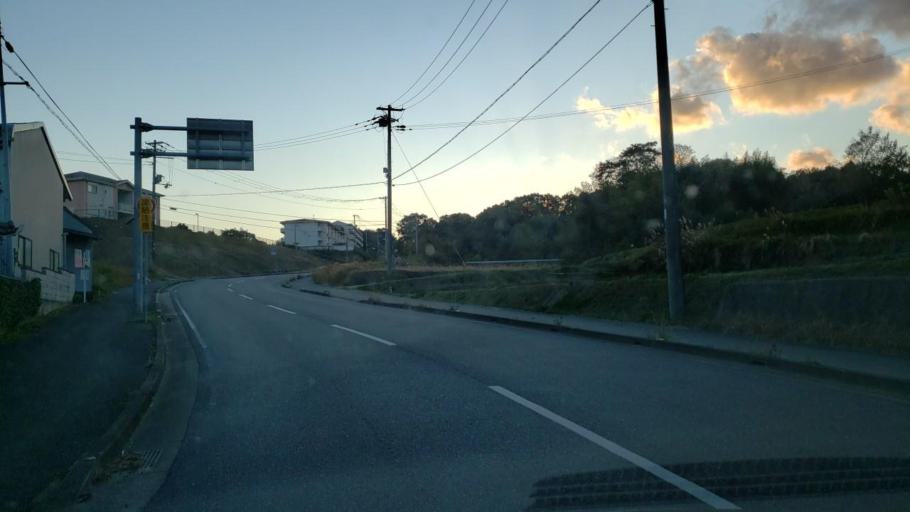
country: JP
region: Hyogo
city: Sumoto
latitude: 34.3621
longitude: 134.7890
